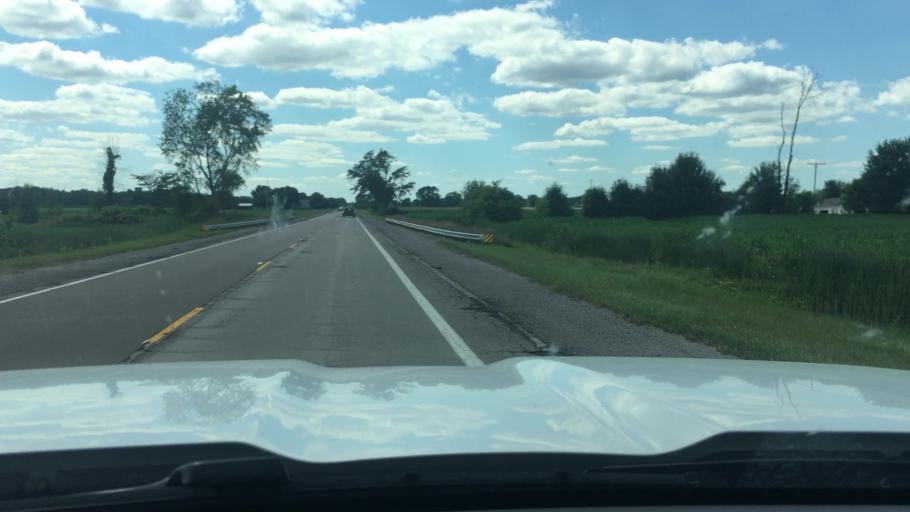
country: US
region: Michigan
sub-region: Saginaw County
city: Chesaning
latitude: 43.1869
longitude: -84.2376
